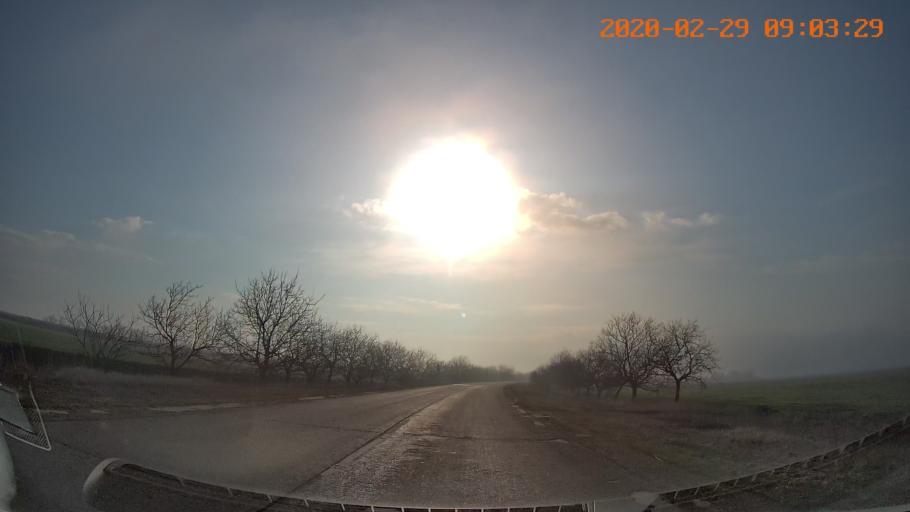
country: UA
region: Odessa
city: Velykoploske
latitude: 46.9154
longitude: 29.7293
